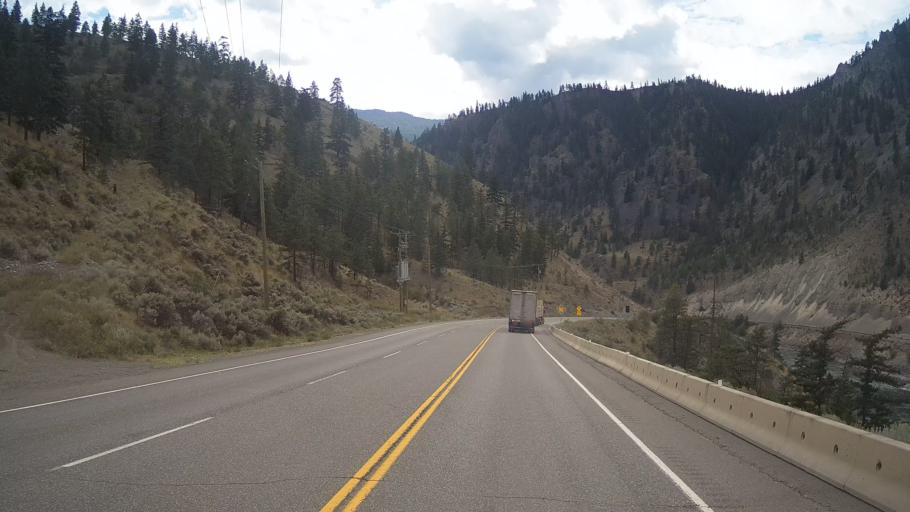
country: CA
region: British Columbia
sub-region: Thompson-Nicola Regional District
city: Ashcroft
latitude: 50.2838
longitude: -121.4032
